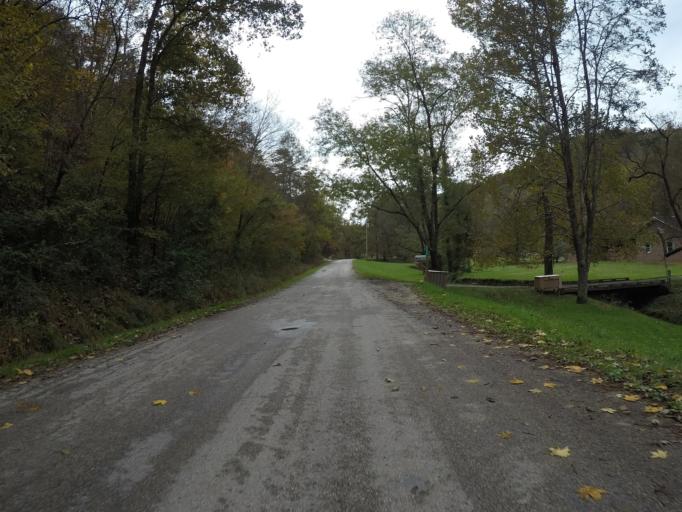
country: US
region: West Virginia
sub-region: Wayne County
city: Lavalette
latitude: 38.3509
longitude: -82.4202
